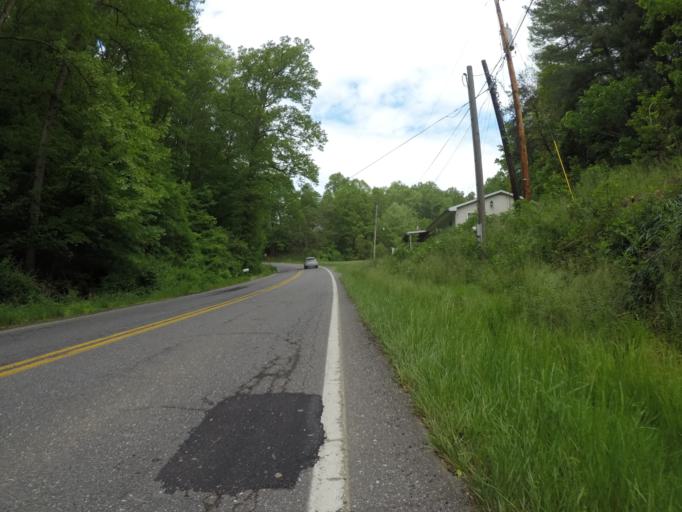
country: US
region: West Virginia
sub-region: Wayne County
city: Ceredo
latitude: 38.3550
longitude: -82.5487
